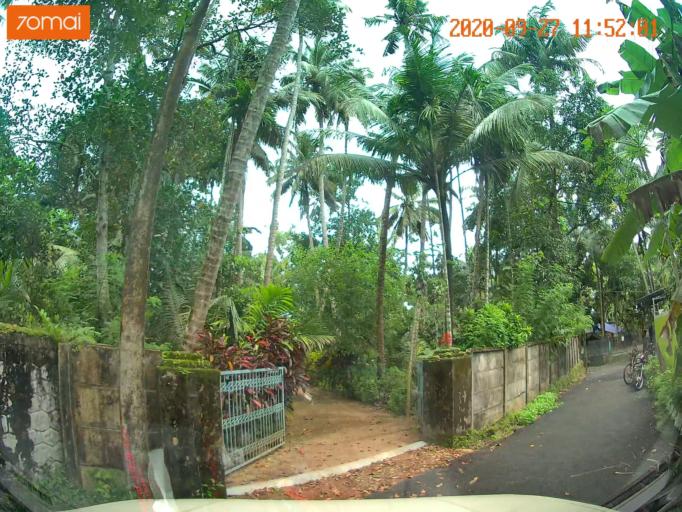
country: IN
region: Kerala
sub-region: Thrissur District
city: Thanniyam
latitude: 10.4733
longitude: 76.1170
